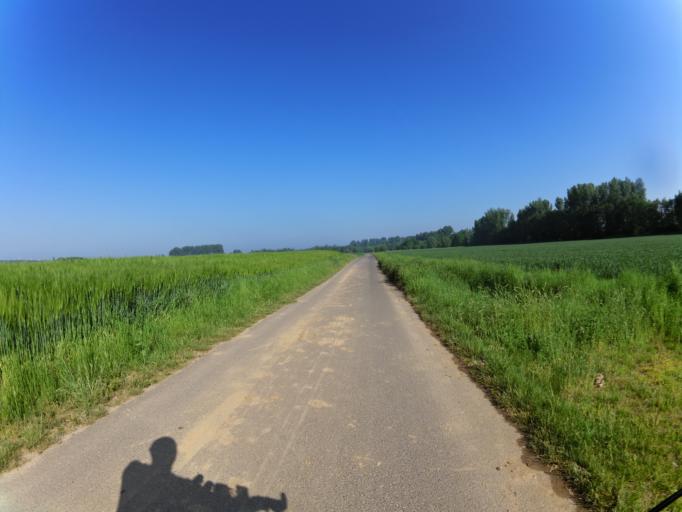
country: DE
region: North Rhine-Westphalia
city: Julich
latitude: 50.9397
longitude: 6.3346
